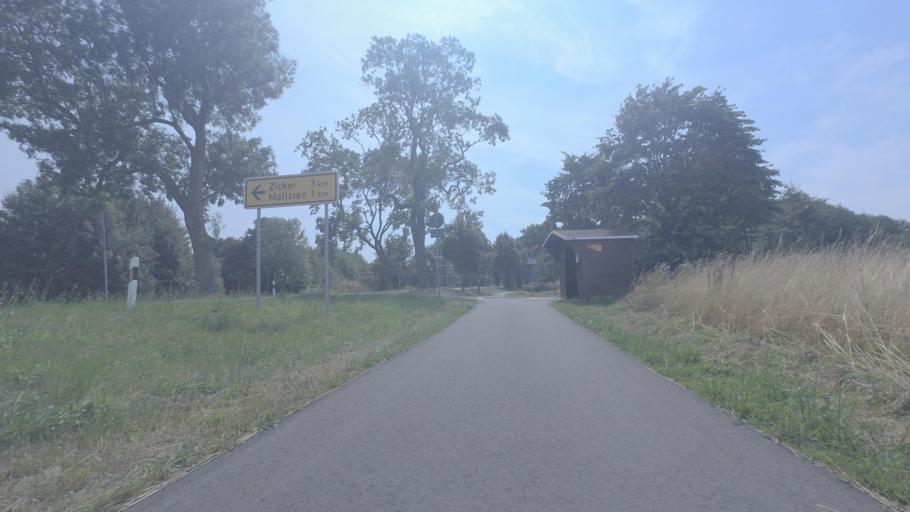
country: DE
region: Mecklenburg-Vorpommern
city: Garz
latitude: 54.2535
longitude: 13.3489
